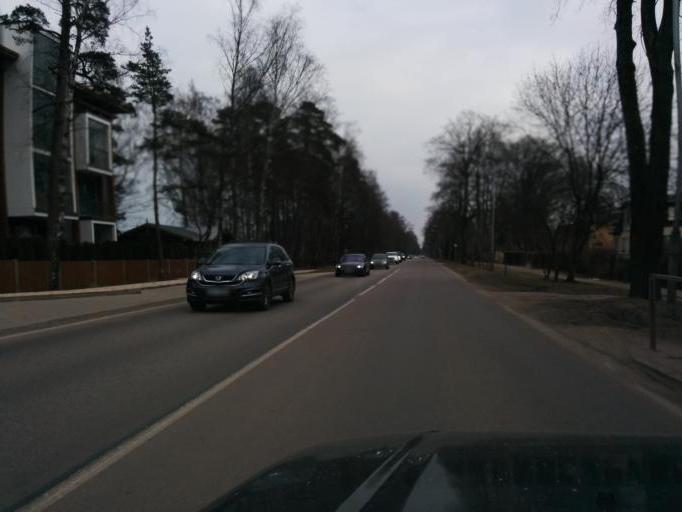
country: LV
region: Jurmala
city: Jurmala
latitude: 56.9581
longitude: 23.6716
